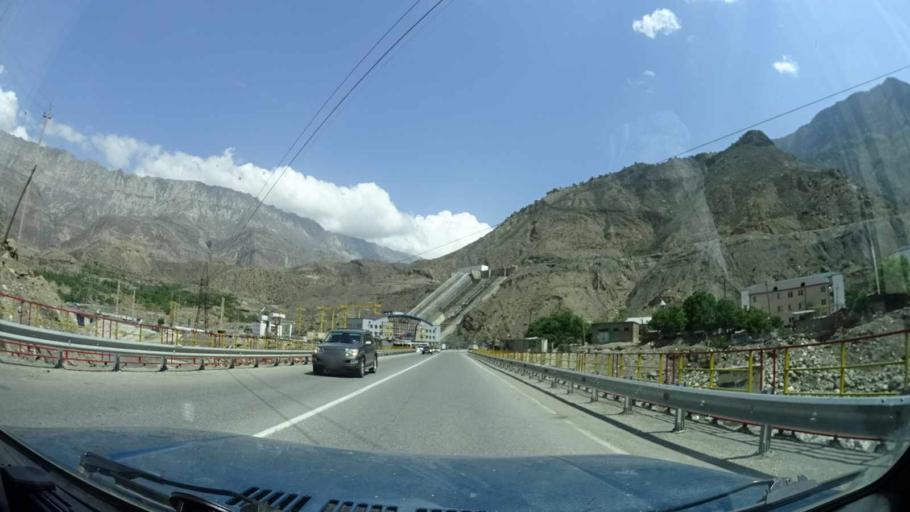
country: RU
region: Dagestan
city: Gimry
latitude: 42.7445
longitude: 46.8285
